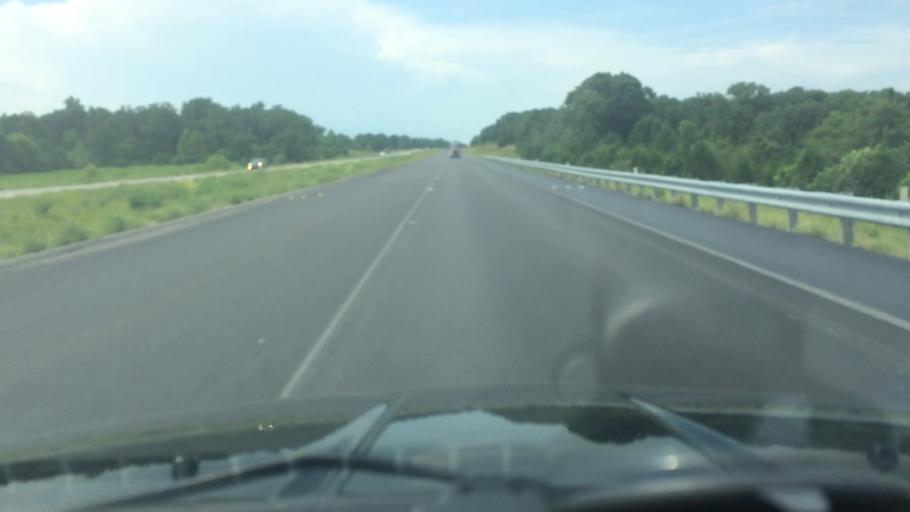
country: US
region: Missouri
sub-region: Saint Clair County
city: Osceola
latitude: 37.9456
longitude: -93.6363
